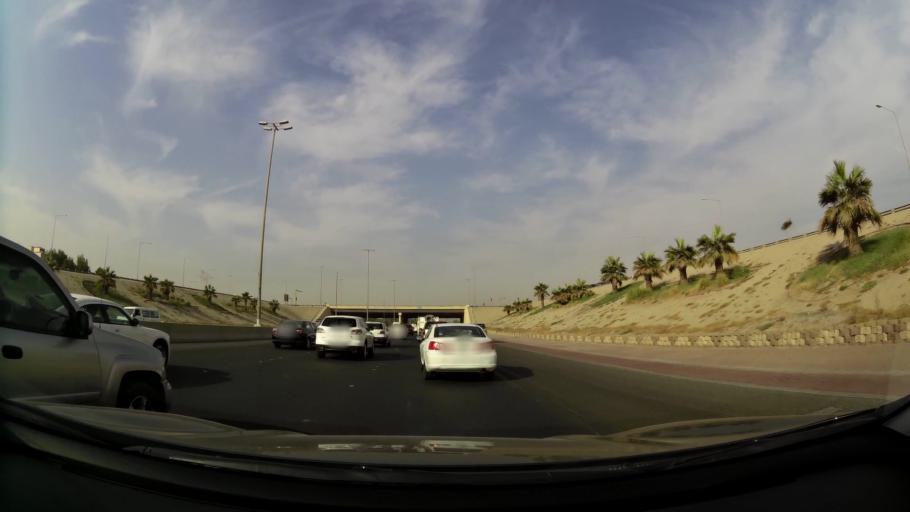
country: KW
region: Mubarak al Kabir
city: Sabah as Salim
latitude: 29.2653
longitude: 48.0689
